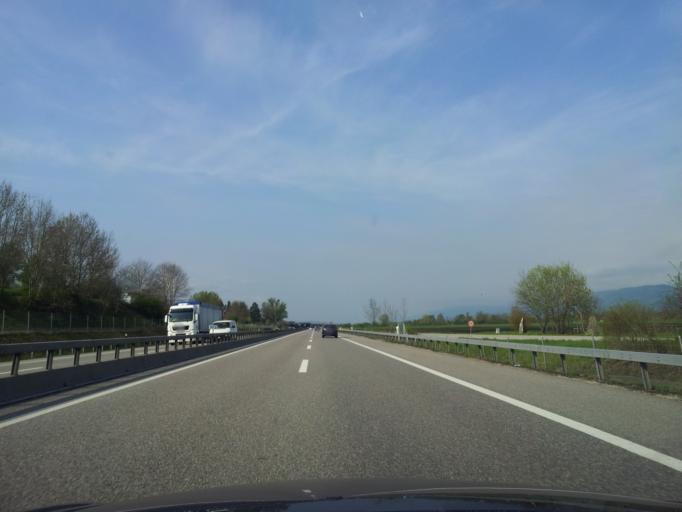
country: CH
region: Bern
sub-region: Seeland District
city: Leuzigen
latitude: 47.1830
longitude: 7.4608
